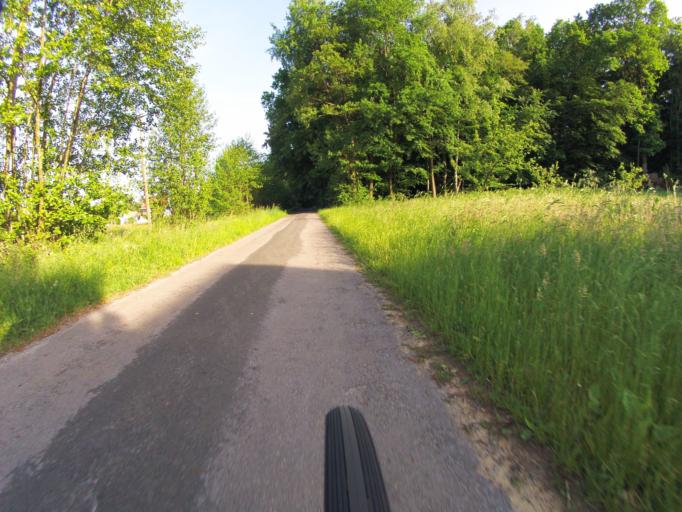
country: DE
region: North Rhine-Westphalia
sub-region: Regierungsbezirk Munster
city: Birgte
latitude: 52.2743
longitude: 7.6549
